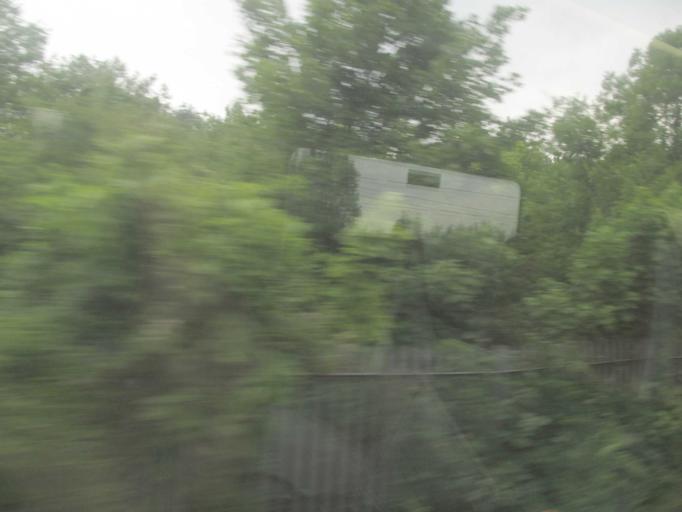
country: GB
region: England
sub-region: Bedford
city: Bedford
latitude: 52.1270
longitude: -0.4775
